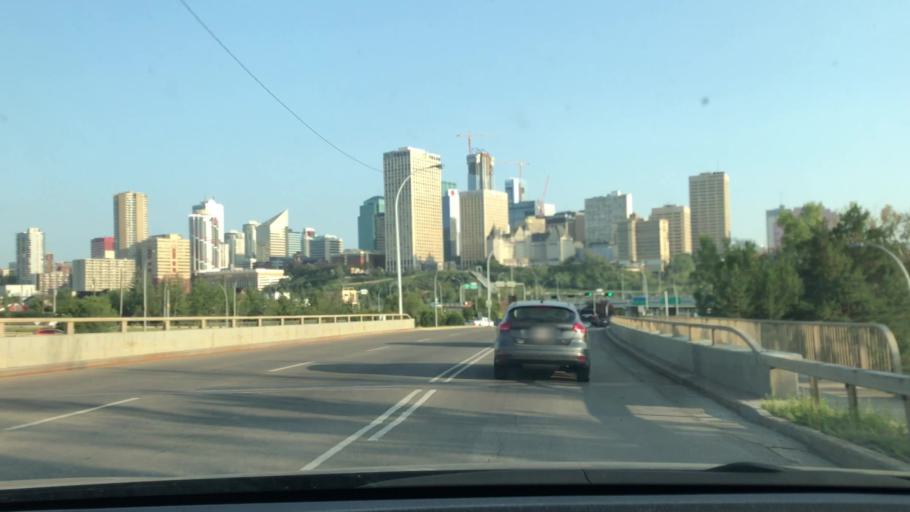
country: CA
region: Alberta
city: Edmonton
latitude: 53.5337
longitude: -113.4822
